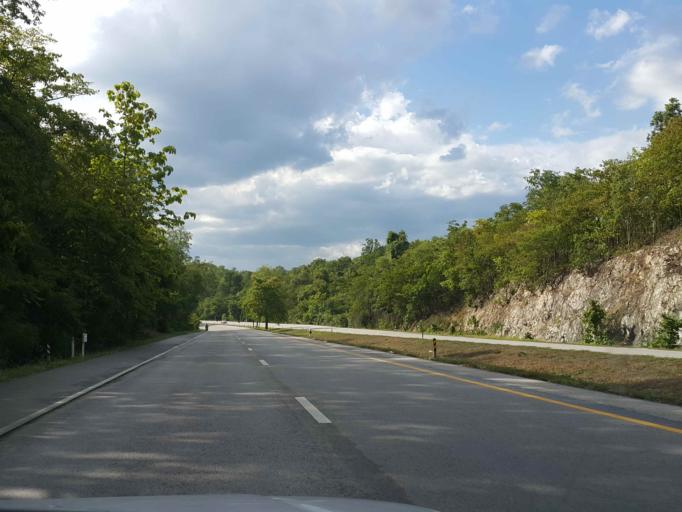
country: TH
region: Lampang
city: Thoen
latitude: 17.6839
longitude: 99.2399
